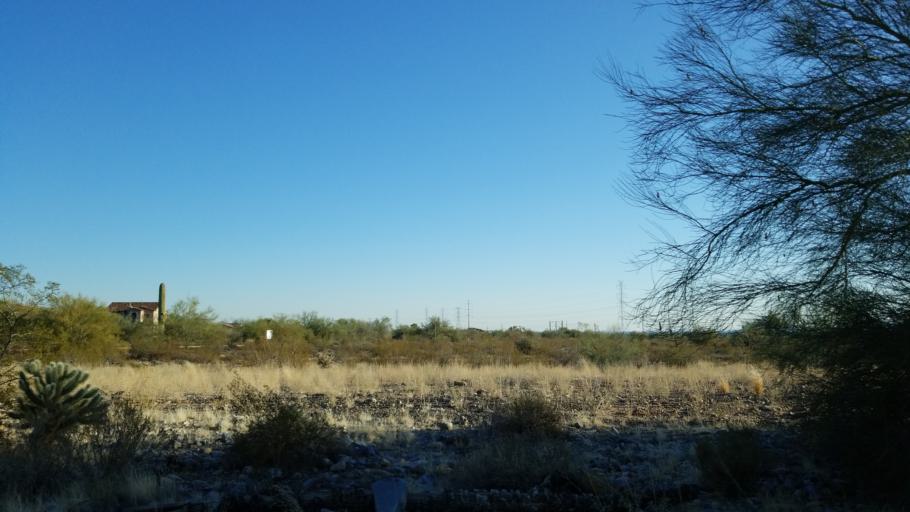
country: US
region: Arizona
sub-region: Maricopa County
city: Paradise Valley
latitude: 33.6503
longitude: -111.8858
